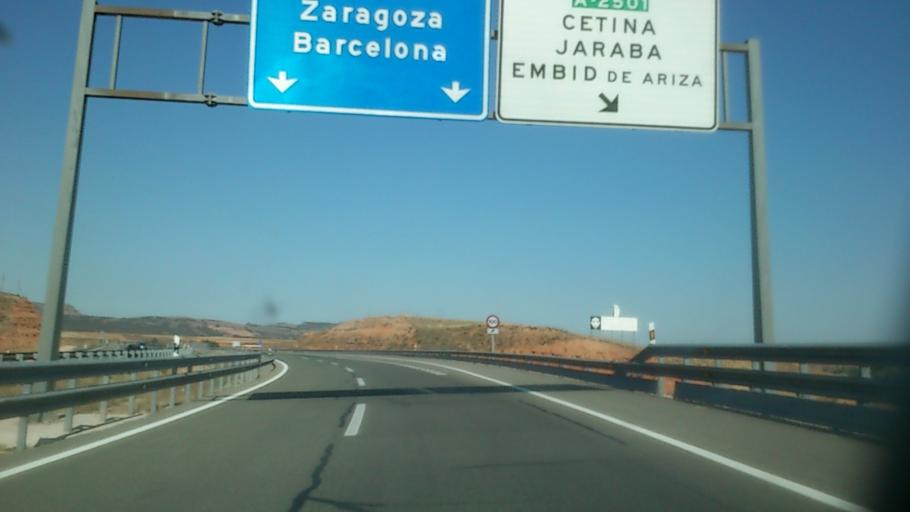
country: ES
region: Aragon
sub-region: Provincia de Zaragoza
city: Cetina
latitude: 41.3046
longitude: -1.9732
